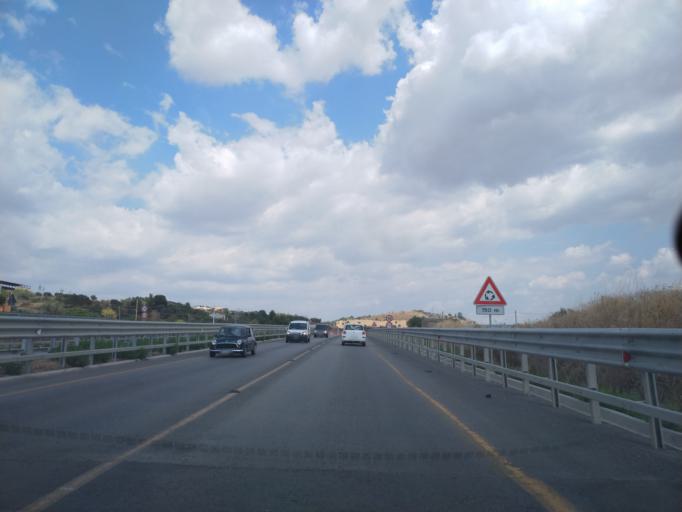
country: IT
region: Sicily
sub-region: Provincia di Caltanissetta
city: San Cataldo
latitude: 37.4536
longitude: 13.9814
